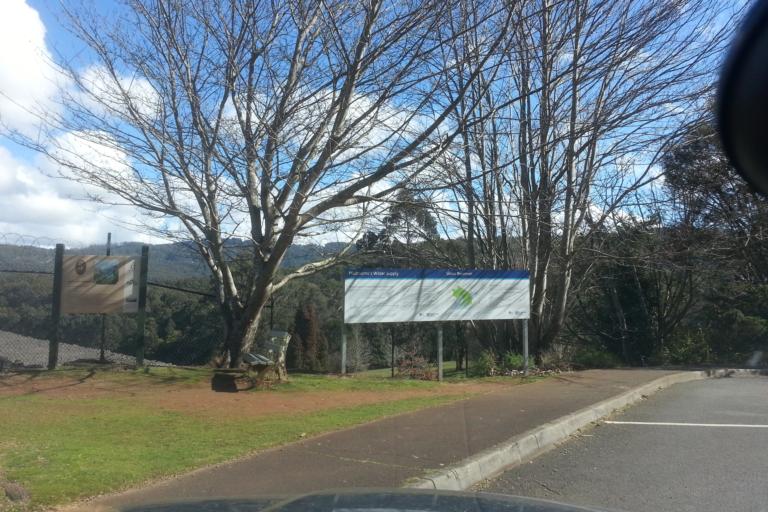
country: AU
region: Victoria
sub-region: Yarra Ranges
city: Mount Dandenong
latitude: -37.8264
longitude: 145.4086
